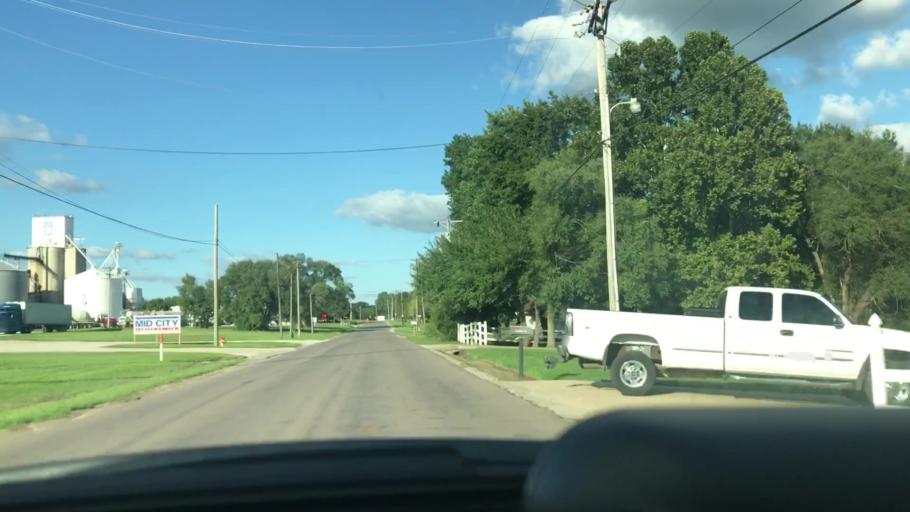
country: US
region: Missouri
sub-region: Pettis County
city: Sedalia
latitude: 38.6901
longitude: -93.2427
